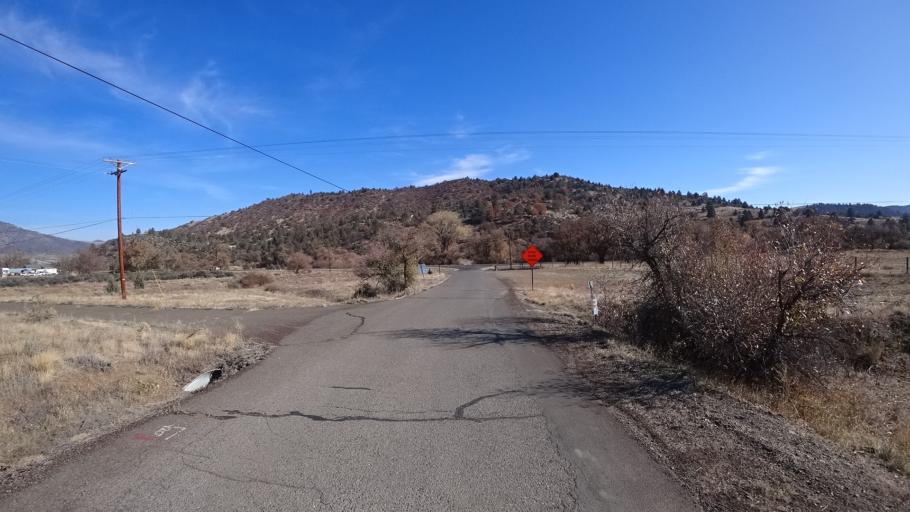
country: US
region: California
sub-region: Siskiyou County
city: Yreka
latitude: 41.7595
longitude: -122.6250
